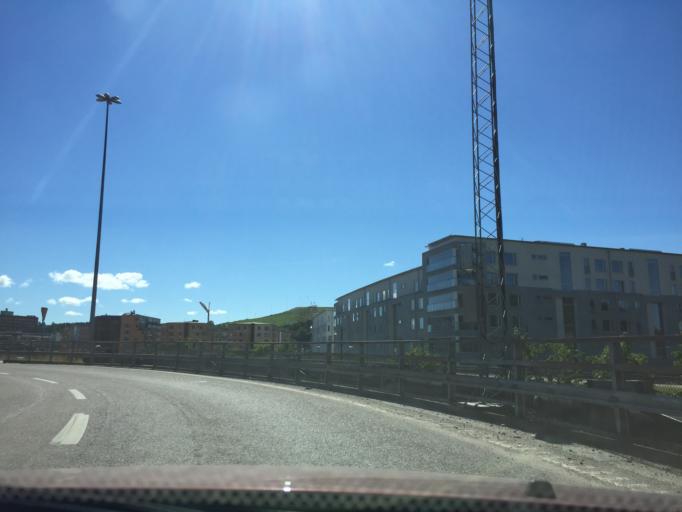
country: SE
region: Stockholm
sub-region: Stockholms Kommun
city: OEstermalm
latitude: 59.3083
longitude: 18.1119
